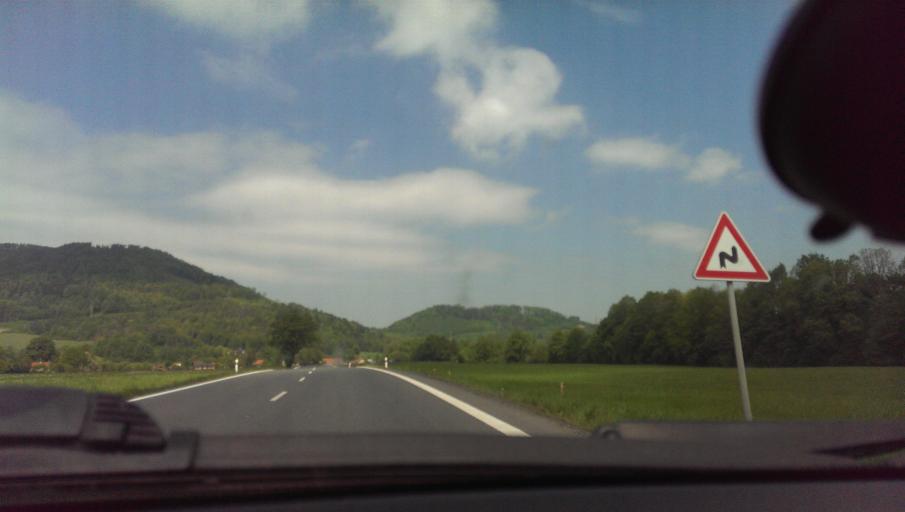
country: CZ
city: Lichnov (o. Novy Jicin)
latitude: 49.5671
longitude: 18.1874
